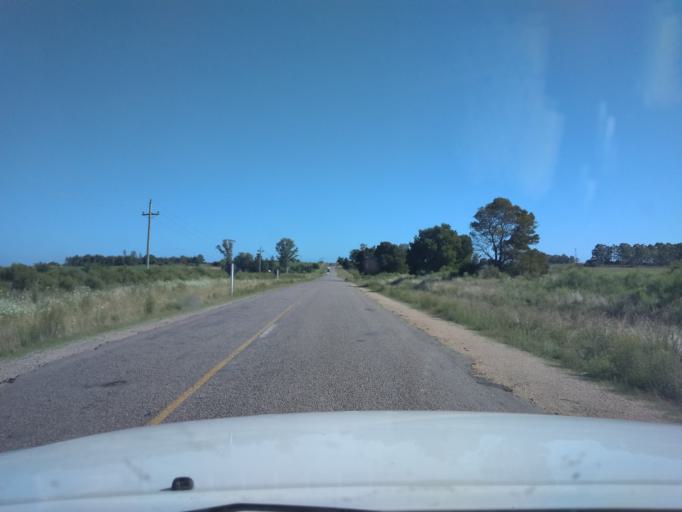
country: UY
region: Canelones
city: San Ramon
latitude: -34.2591
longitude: -55.9269
